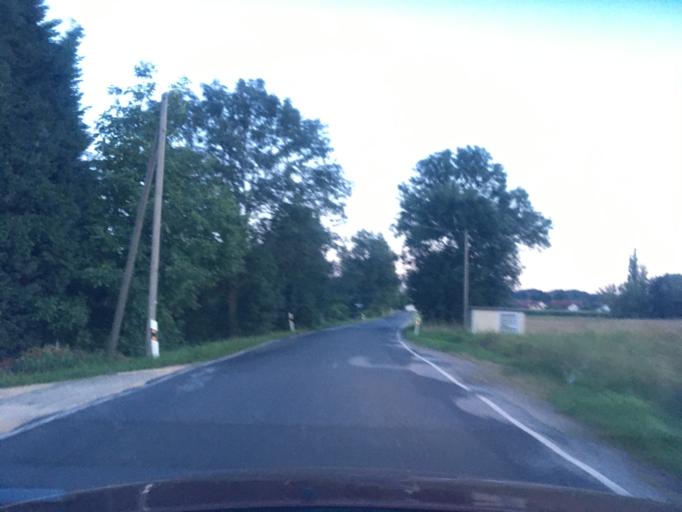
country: DE
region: Saxony
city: Goerlitz
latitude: 51.2024
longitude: 14.9981
